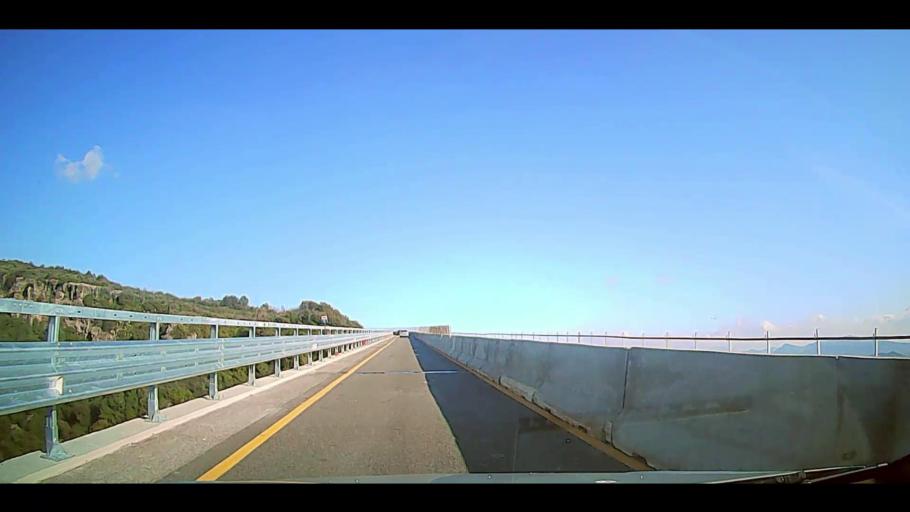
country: IT
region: Calabria
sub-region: Provincia di Crotone
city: Caccuri
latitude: 39.2239
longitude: 16.7946
